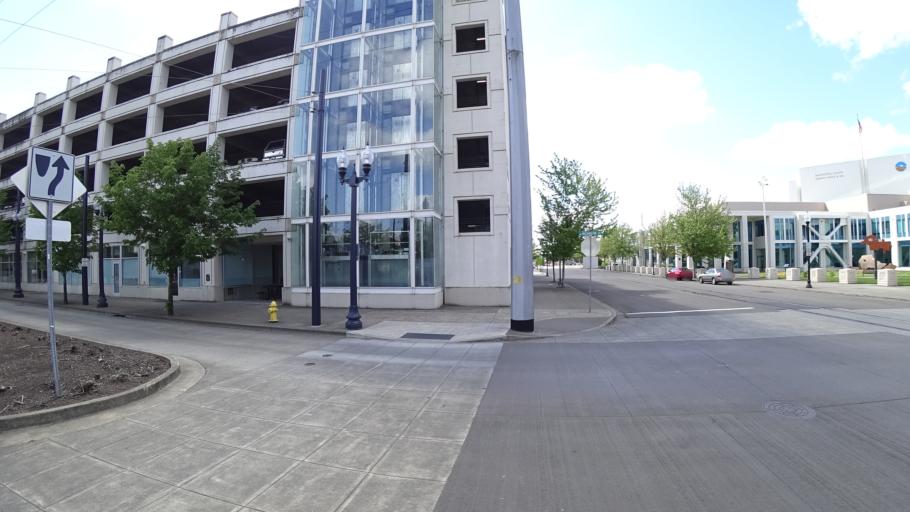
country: US
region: Oregon
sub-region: Washington County
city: Hillsboro
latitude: 45.5214
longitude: -122.9911
